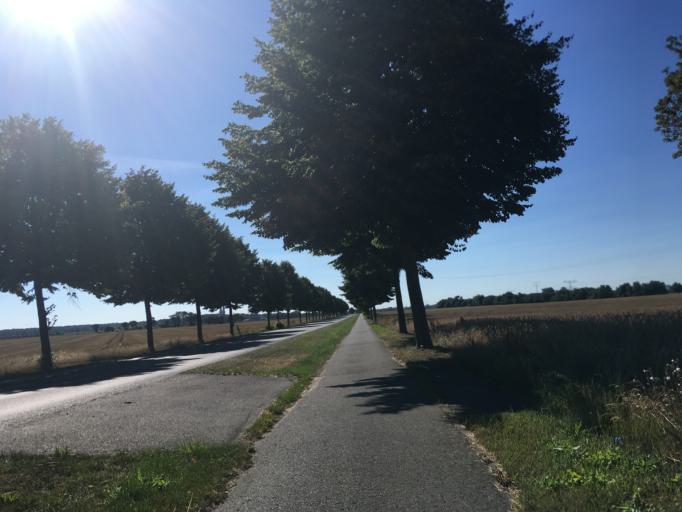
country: DE
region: Berlin
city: Falkenberg
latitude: 52.5960
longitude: 13.5417
